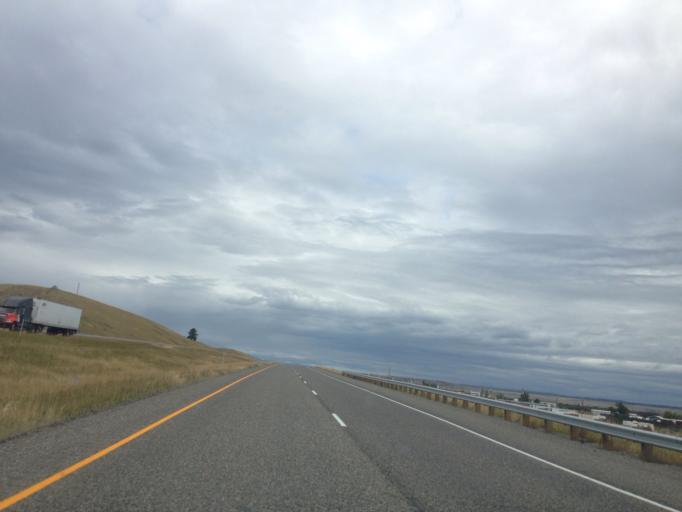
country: US
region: Montana
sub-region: Sweet Grass County
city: Big Timber
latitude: 45.7484
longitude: -109.7744
